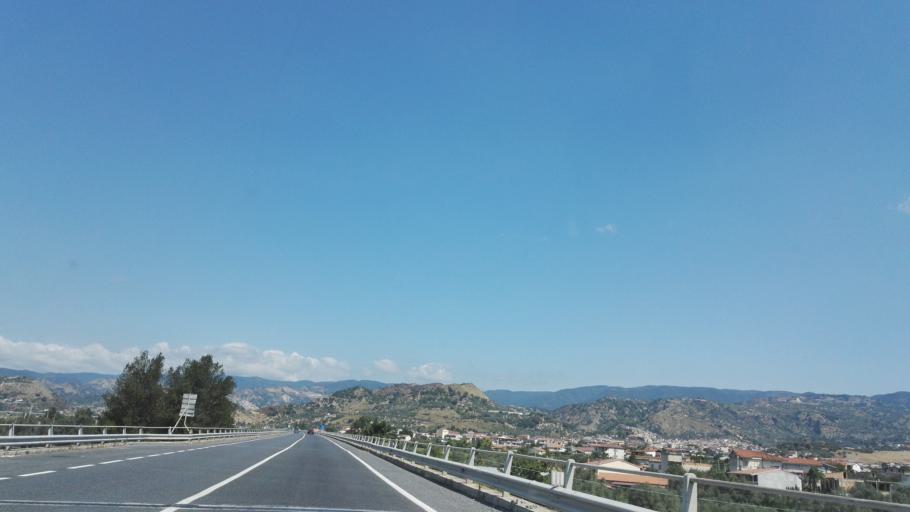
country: IT
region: Calabria
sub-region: Provincia di Reggio Calabria
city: Gioiosa Ionica
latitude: 38.3142
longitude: 16.3021
